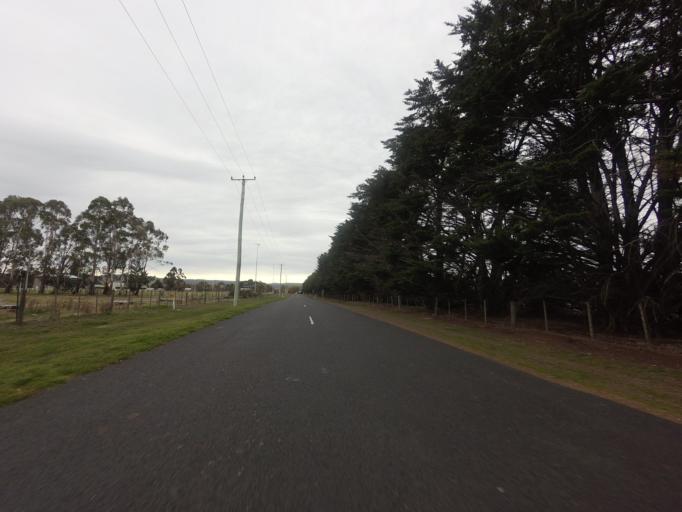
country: AU
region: Tasmania
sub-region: Derwent Valley
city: New Norfolk
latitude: -42.3891
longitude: 147.0063
